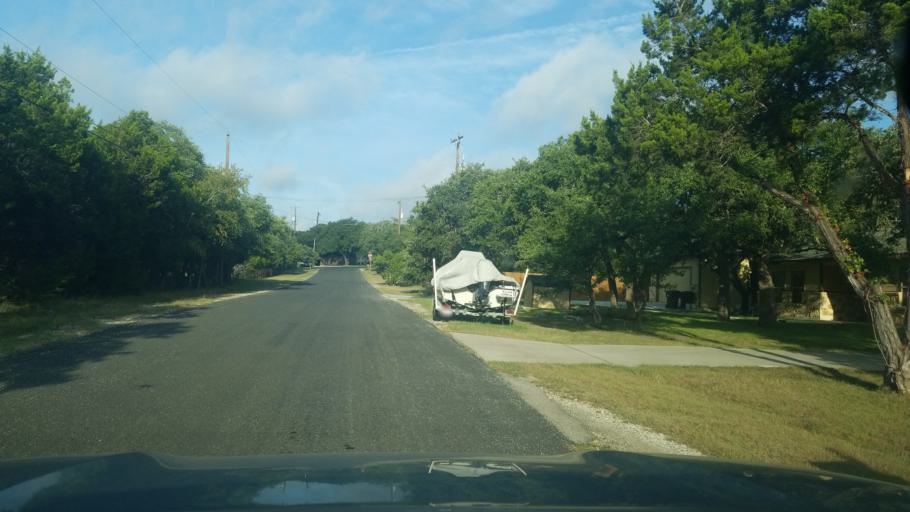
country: US
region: Texas
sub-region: Bexar County
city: Timberwood Park
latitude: 29.6989
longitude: -98.5126
